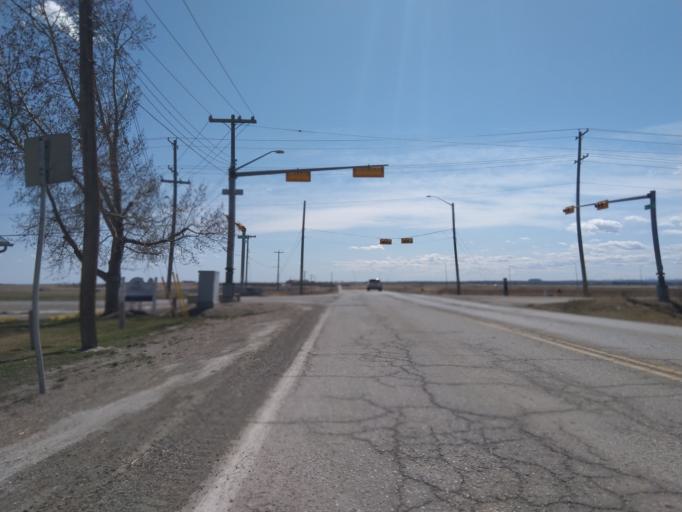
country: CA
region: Alberta
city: Chestermere
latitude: 50.9509
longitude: -113.9119
